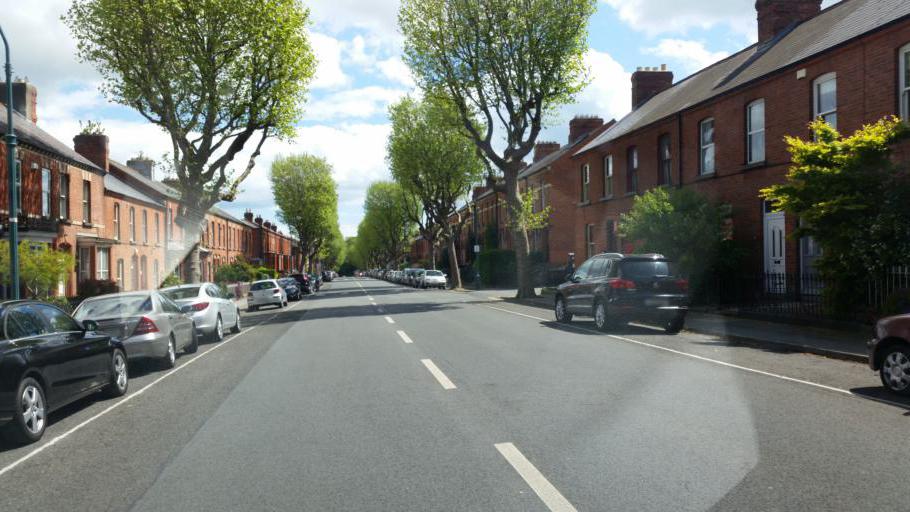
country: IE
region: Leinster
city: Drumcondra
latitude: 53.3678
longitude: -6.2613
